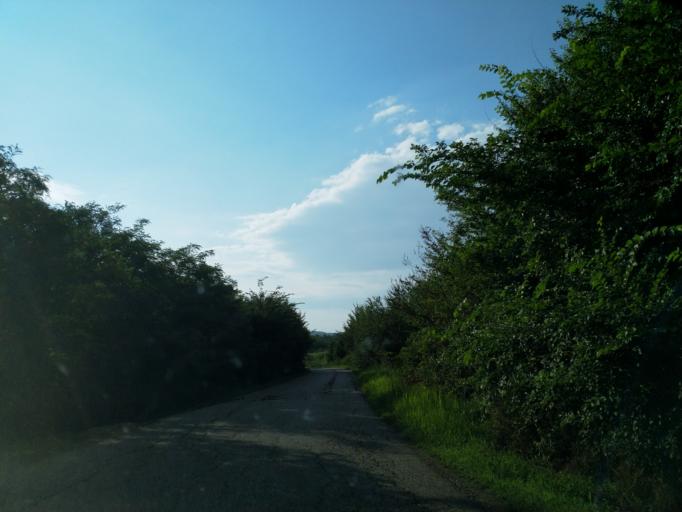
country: RS
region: Central Serbia
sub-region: Pomoravski Okrug
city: Jagodina
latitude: 43.9935
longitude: 21.1990
